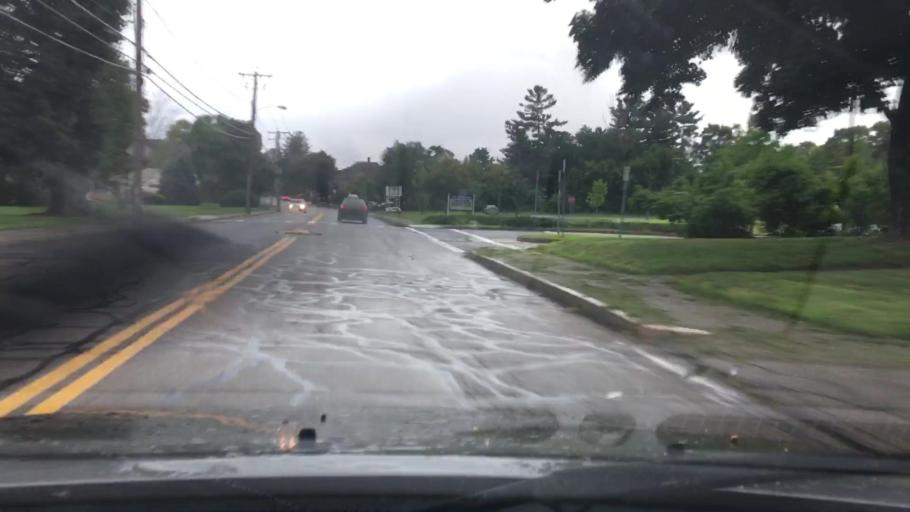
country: US
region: Massachusetts
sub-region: Worcester County
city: Milford
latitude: 42.1513
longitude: -71.5279
